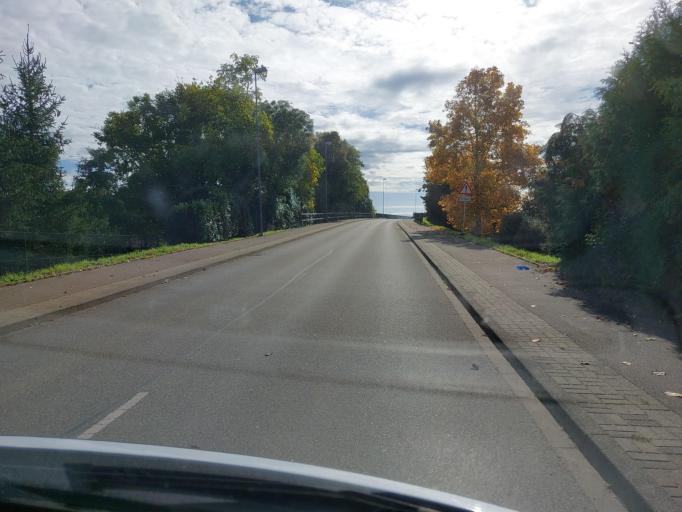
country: DE
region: Baden-Wuerttemberg
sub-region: Freiburg Region
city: Teningen
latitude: 48.1377
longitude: 7.8056
